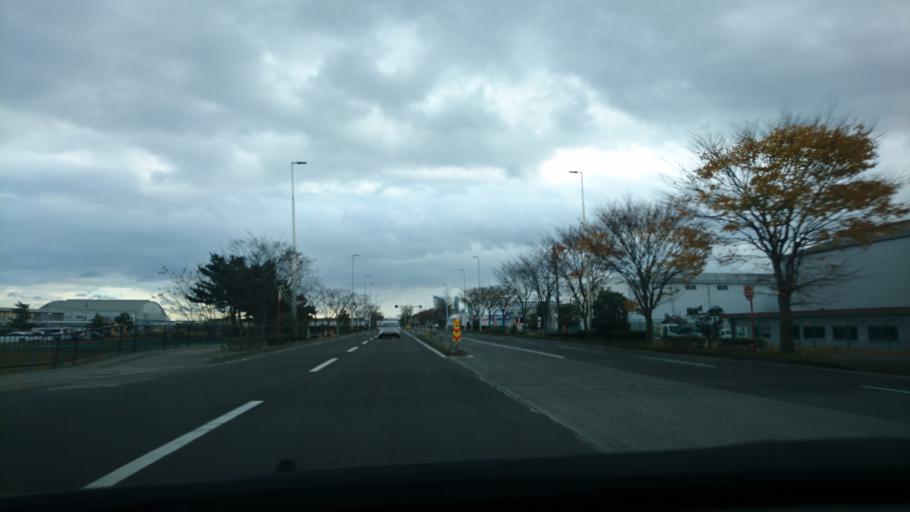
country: JP
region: Miyagi
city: Iwanuma
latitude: 38.1321
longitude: 140.9173
